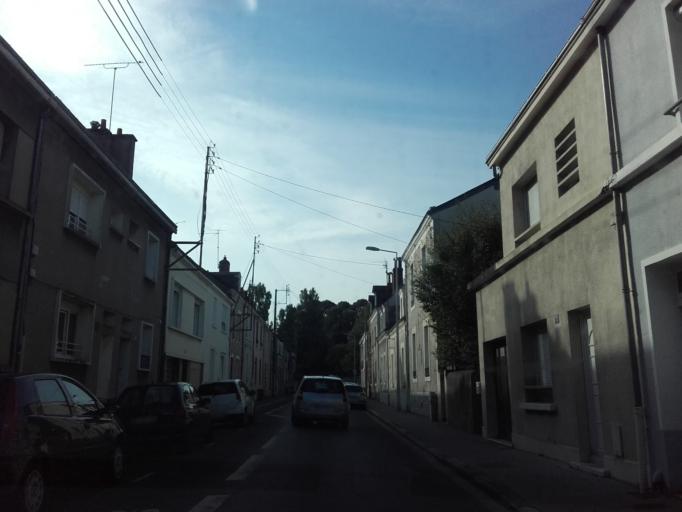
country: FR
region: Centre
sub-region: Departement d'Indre-et-Loire
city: Tours
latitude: 47.3836
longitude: 0.7041
